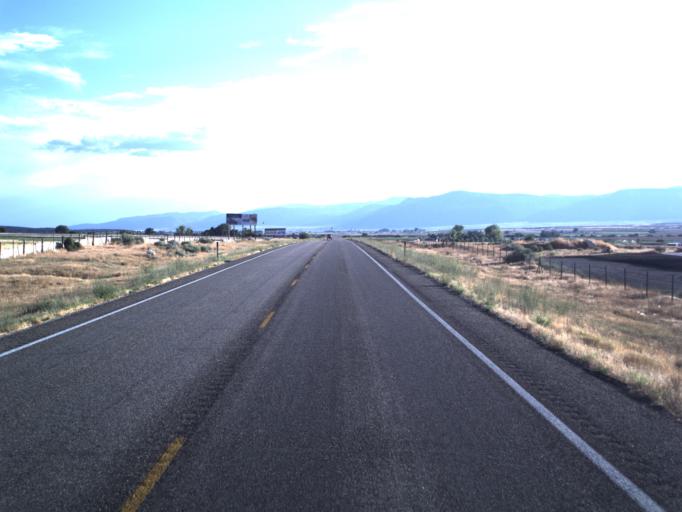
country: US
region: Utah
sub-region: Sanpete County
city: Mount Pleasant
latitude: 39.5243
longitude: -111.4753
